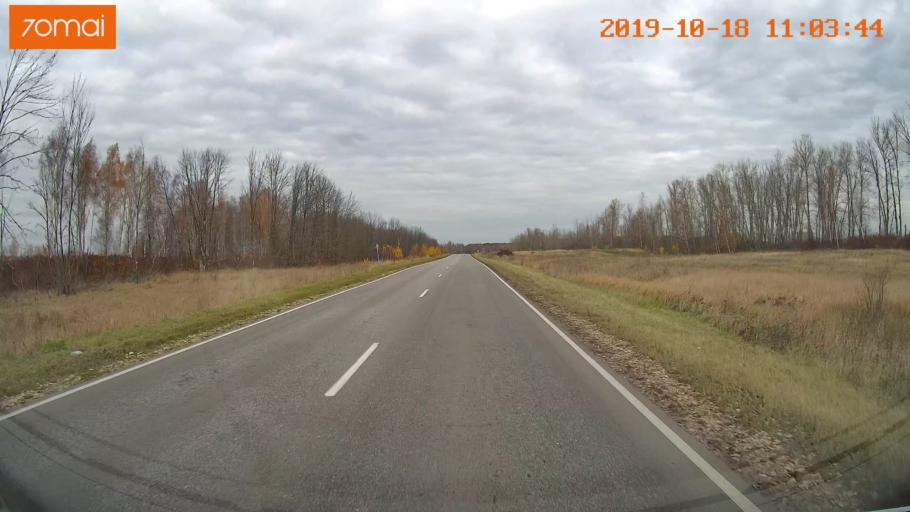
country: RU
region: Tula
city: Yepifan'
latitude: 53.8842
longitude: 38.5493
